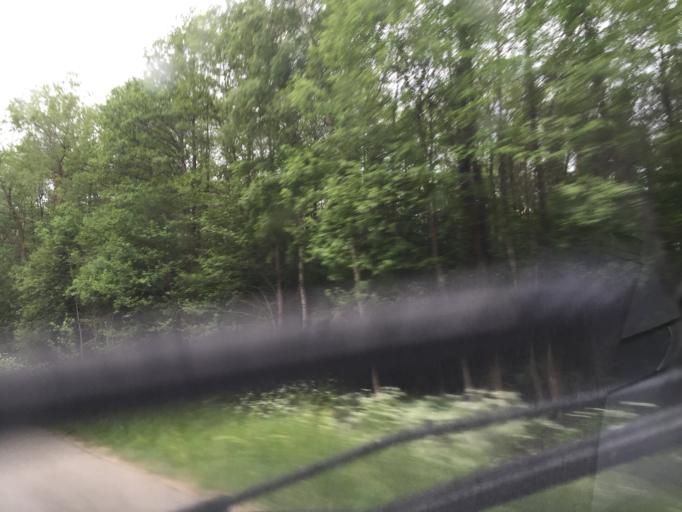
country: LT
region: Klaipedos apskritis
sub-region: Klaipeda
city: Palanga
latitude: 55.8178
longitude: 21.0730
